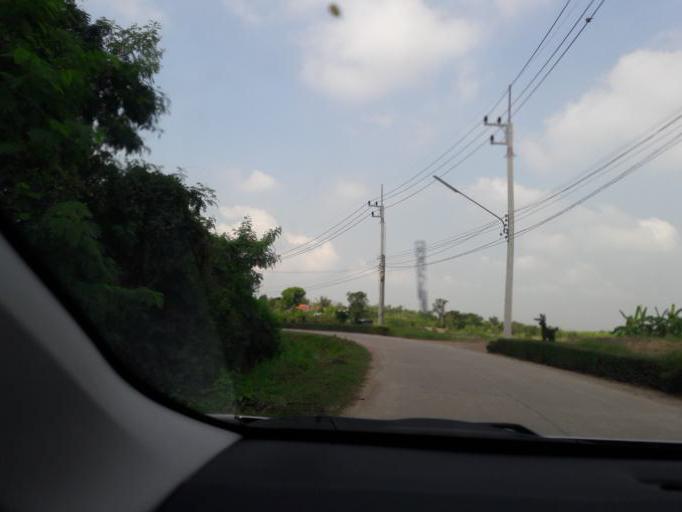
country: TH
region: Ang Thong
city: Ang Thong
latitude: 14.5490
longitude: 100.4398
